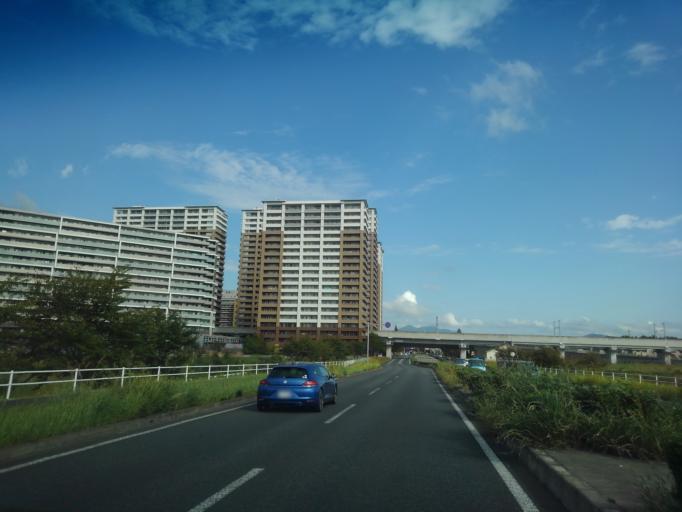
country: JP
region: Ibaraki
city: Naka
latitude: 36.0798
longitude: 140.0859
